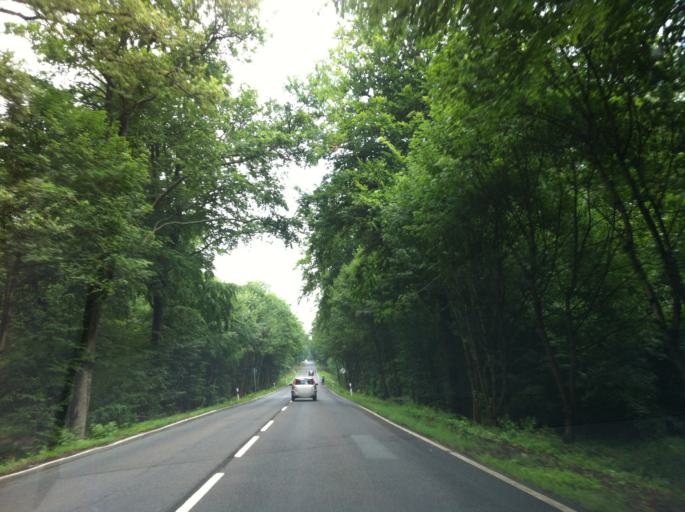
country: DE
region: Hesse
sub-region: Regierungsbezirk Darmstadt
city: Konigstein im Taunus
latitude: 50.1669
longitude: 8.4799
